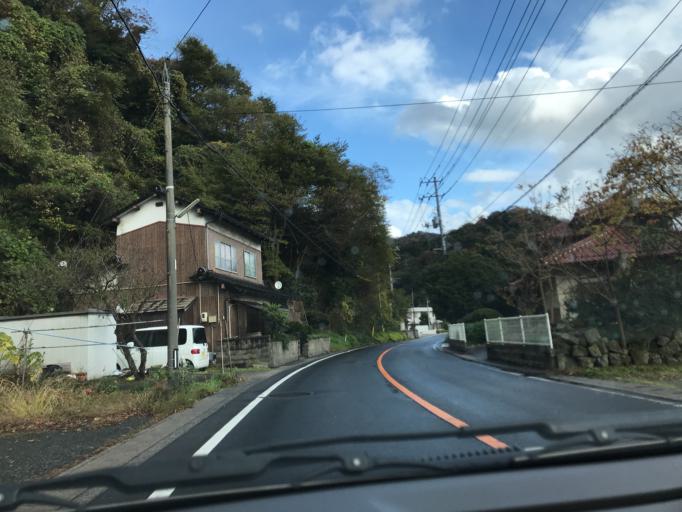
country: JP
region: Shimane
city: Sakaiminato
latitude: 35.5508
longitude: 133.2310
